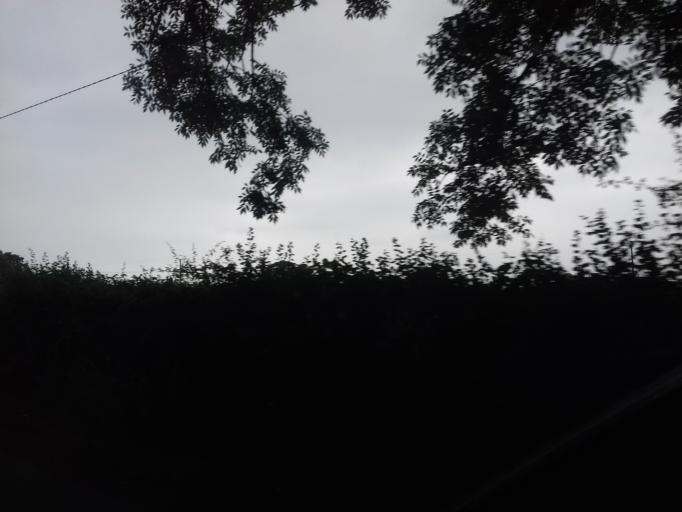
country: IE
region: Leinster
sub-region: Fingal County
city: Swords
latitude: 53.4848
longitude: -6.2453
